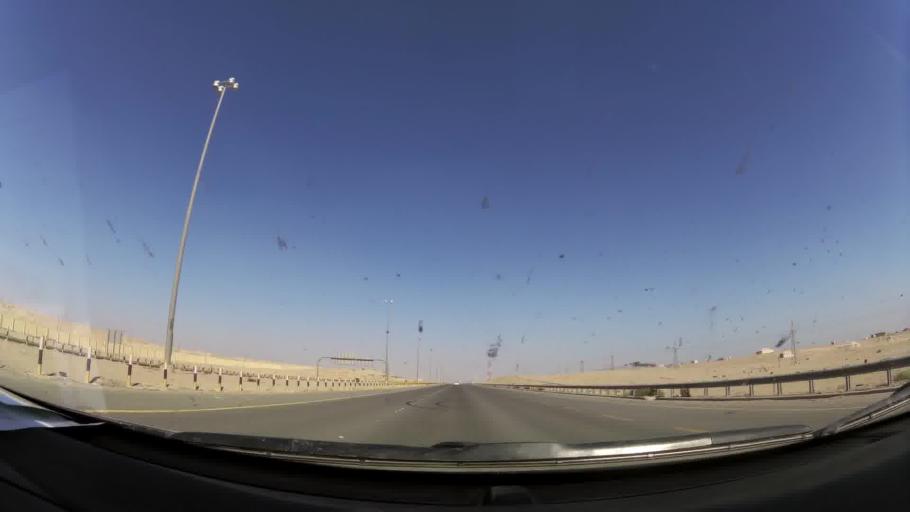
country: KW
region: Muhafazat al Jahra'
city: Al Jahra'
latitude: 29.4120
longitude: 47.7028
